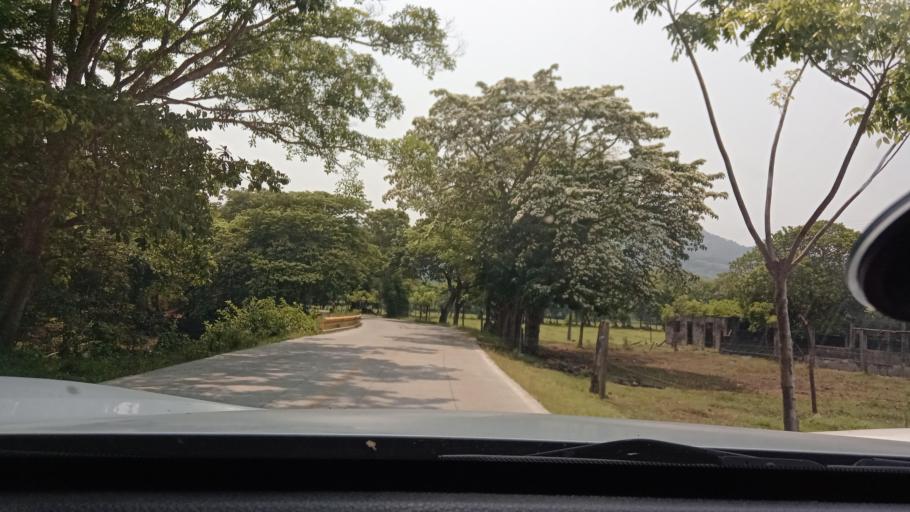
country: MX
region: Veracruz
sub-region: San Andres Tuxtla
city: Santa Rosa Abata
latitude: 18.5628
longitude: -95.0567
